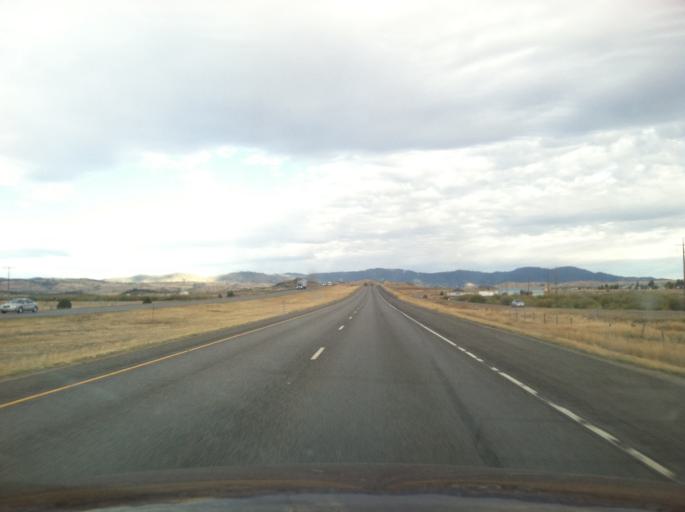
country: US
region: Montana
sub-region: Silver Bow County
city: Butte-Silver Bow (Balance)
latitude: 46.0100
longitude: -112.6976
